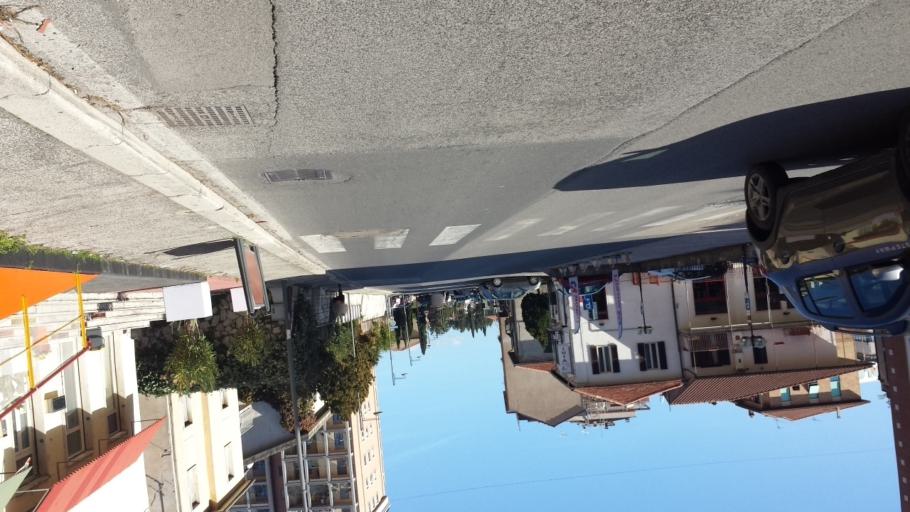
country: IT
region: Umbria
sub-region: Provincia di Terni
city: Terni
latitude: 42.5804
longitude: 12.6241
